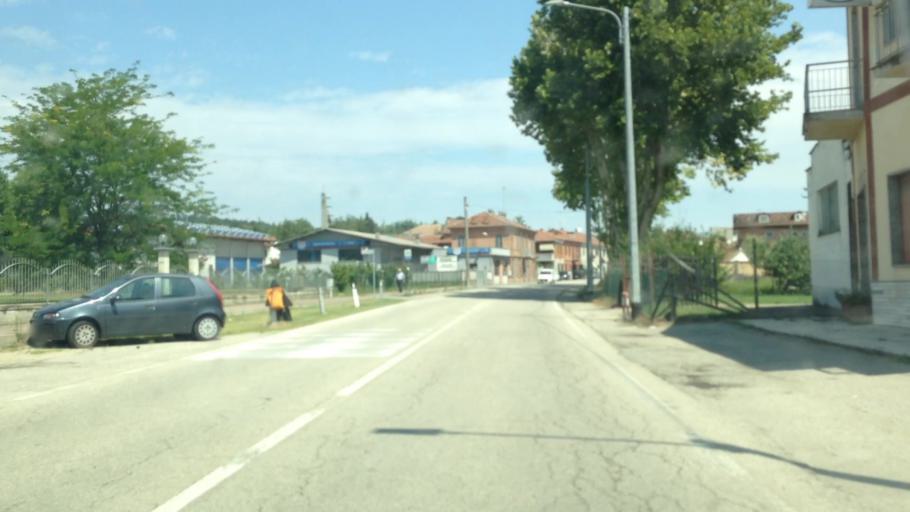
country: IT
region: Piedmont
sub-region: Provincia di Asti
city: Castell'Alfero
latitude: 44.9545
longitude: 8.2231
